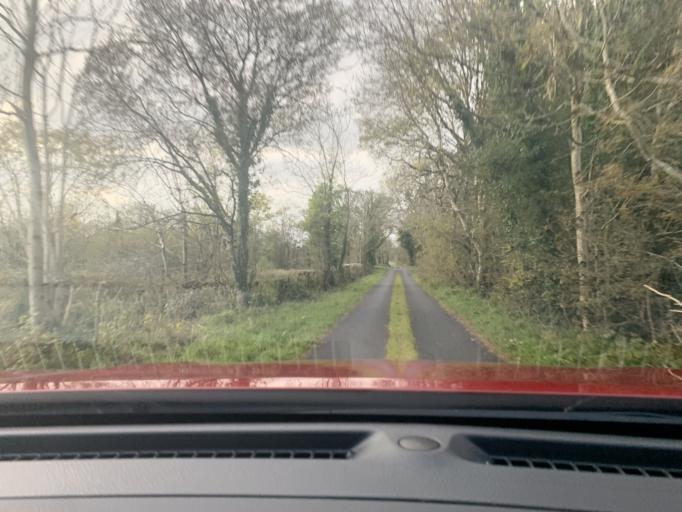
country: IE
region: Connaught
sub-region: Roscommon
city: Ballaghaderreen
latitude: 54.0148
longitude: -8.6162
